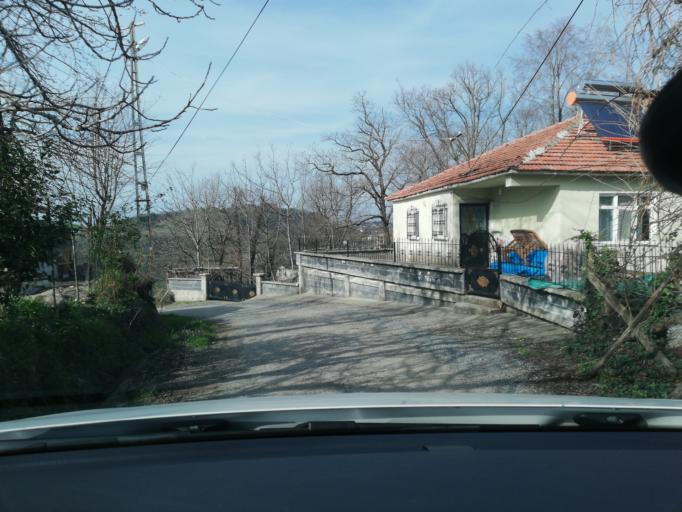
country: TR
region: Zonguldak
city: Kozlu
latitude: 41.3564
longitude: 31.6285
